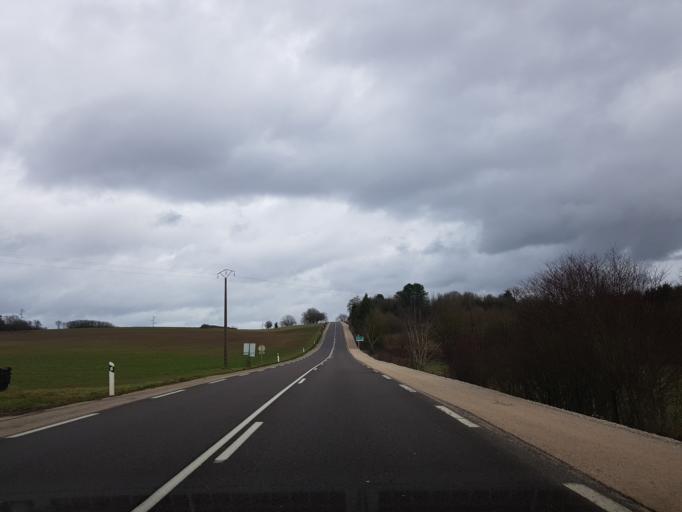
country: FR
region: Franche-Comte
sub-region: Departement de la Haute-Saone
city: Scey-sur-Saone-et-Saint-Albin
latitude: 47.7089
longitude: 5.9018
